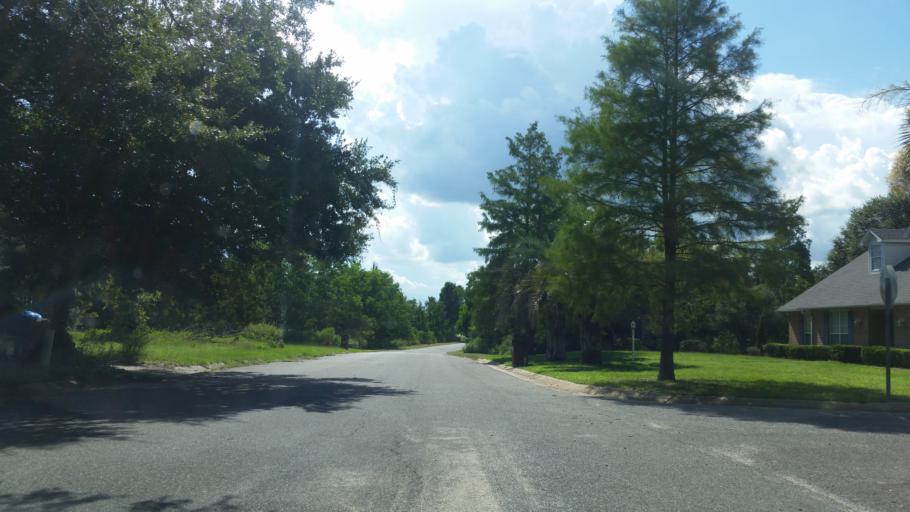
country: US
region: Florida
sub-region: Santa Rosa County
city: Pace
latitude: 30.5817
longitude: -87.1623
